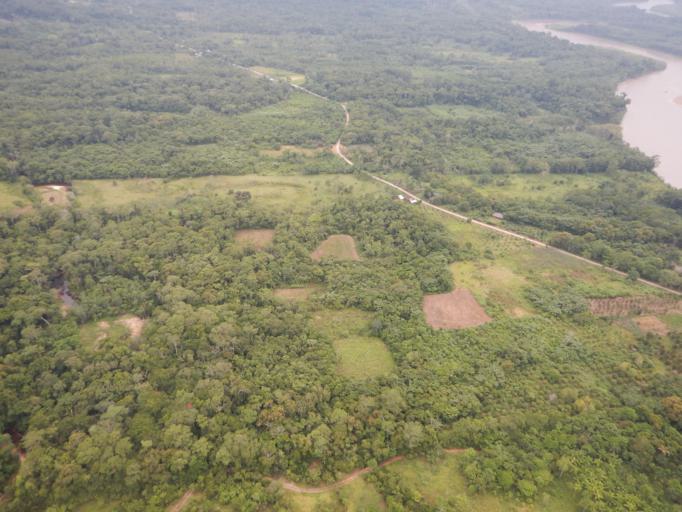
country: BO
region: Cochabamba
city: Chimore
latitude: -17.0748
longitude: -64.8160
